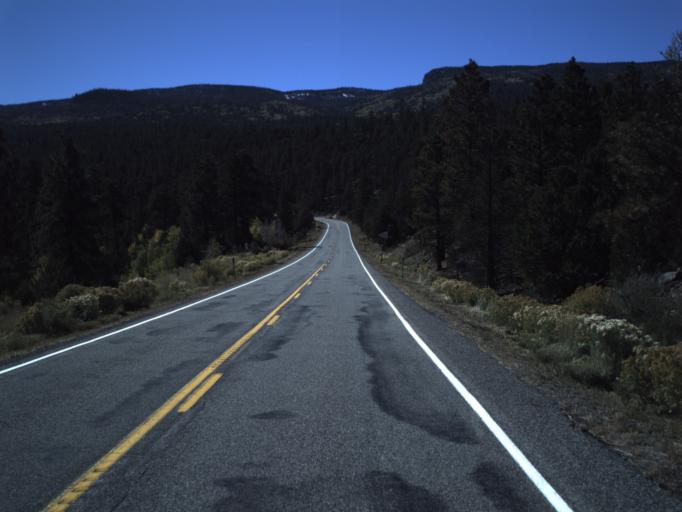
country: US
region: Utah
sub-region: Wayne County
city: Loa
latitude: 38.1923
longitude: -111.3509
